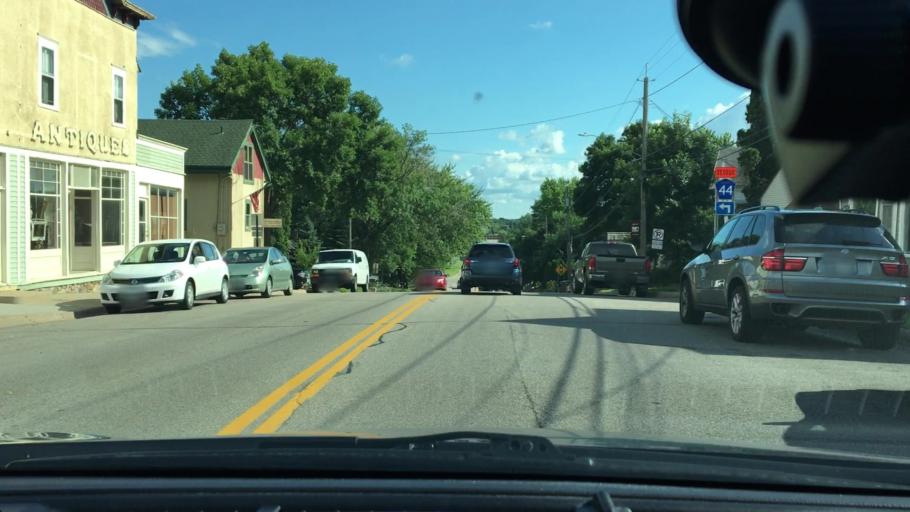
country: US
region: Minnesota
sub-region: Hennepin County
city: Saint Bonifacius
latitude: 44.9039
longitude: -93.7473
